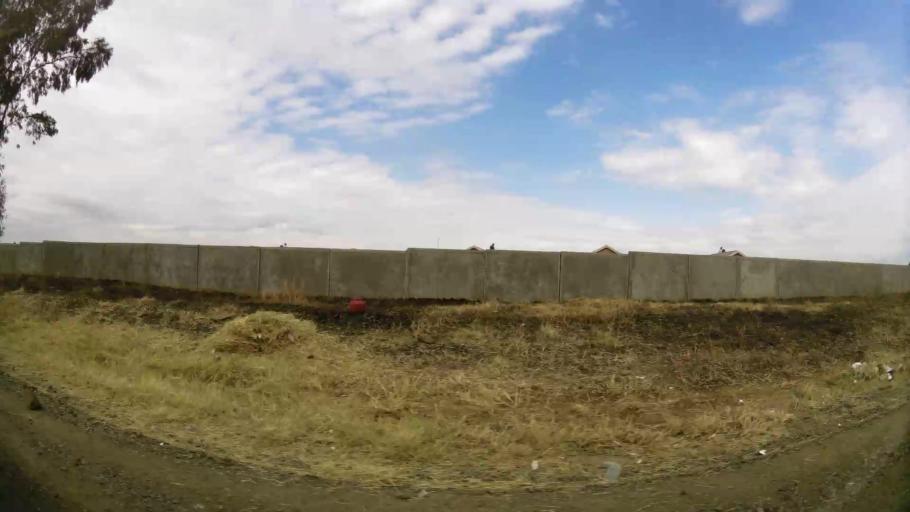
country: ZA
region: Orange Free State
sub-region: Fezile Dabi District Municipality
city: Kroonstad
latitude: -27.6465
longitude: 27.2242
